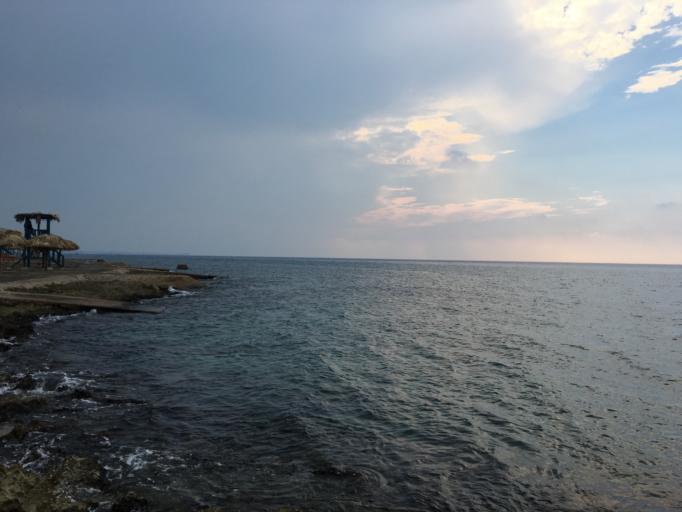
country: CU
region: La Habana
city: Havana
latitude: 23.1148
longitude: -82.4385
